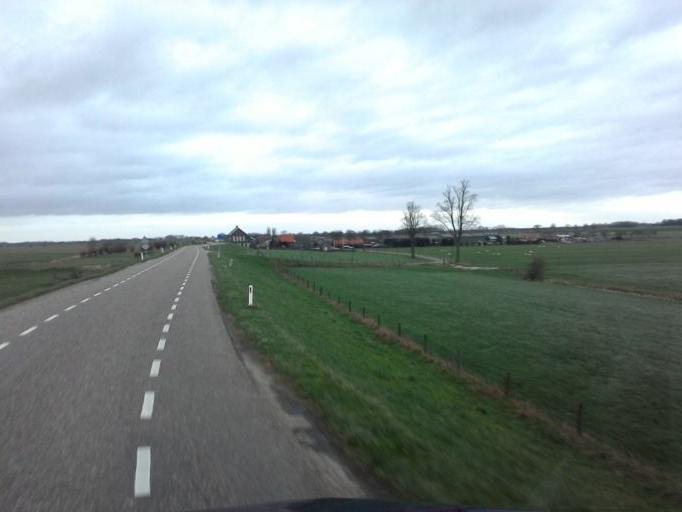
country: NL
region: Gelderland
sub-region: Gemeente Culemborg
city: Culemborg
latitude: 51.9664
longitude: 5.2731
